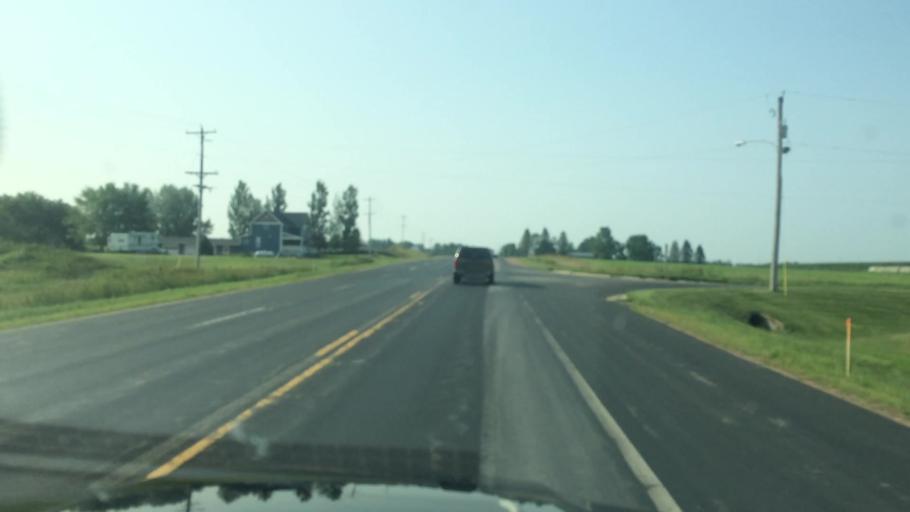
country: US
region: Wisconsin
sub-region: Marathon County
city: Stratford
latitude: 44.8193
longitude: -90.0791
